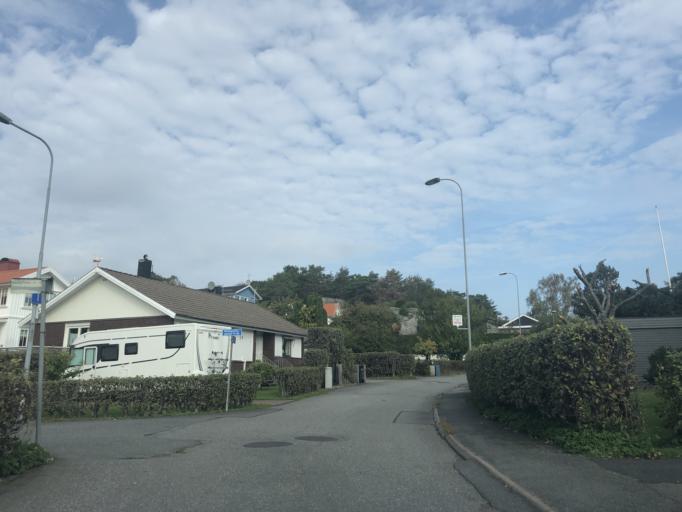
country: SE
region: Vaestra Goetaland
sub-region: Goteborg
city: Majorna
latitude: 57.6550
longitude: 11.8613
